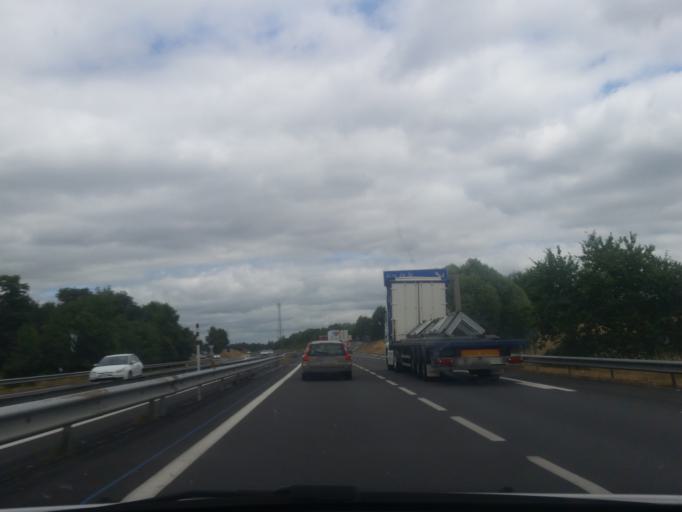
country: FR
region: Pays de la Loire
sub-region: Departement de Maine-et-Loire
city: Durtal
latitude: 47.6205
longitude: -0.2843
